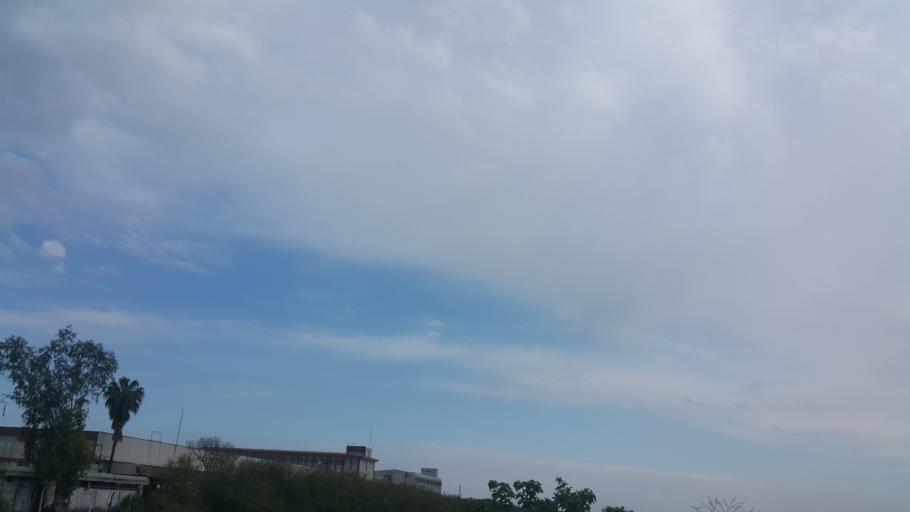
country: TR
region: Mersin
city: Yenice
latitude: 36.9903
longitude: 35.1580
